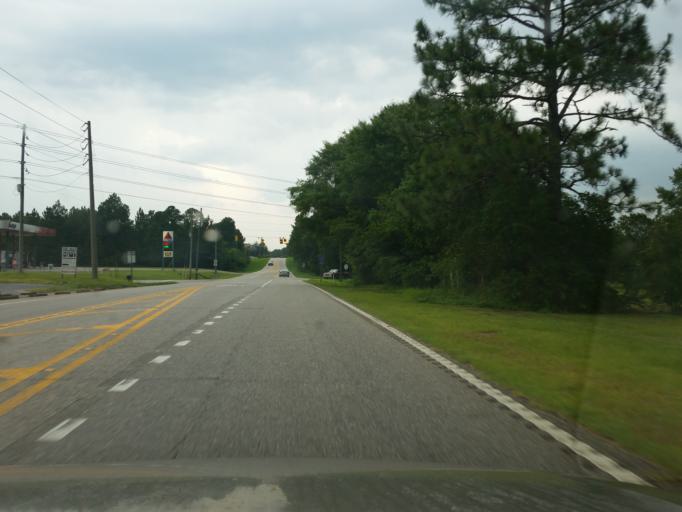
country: US
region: Alabama
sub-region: Baldwin County
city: Robertsdale
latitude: 30.5486
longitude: -87.5809
